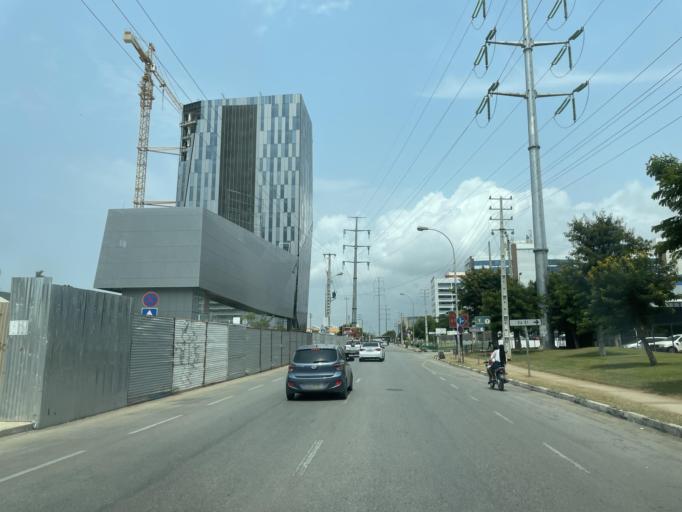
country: AO
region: Luanda
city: Luanda
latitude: -8.9224
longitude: 13.1863
